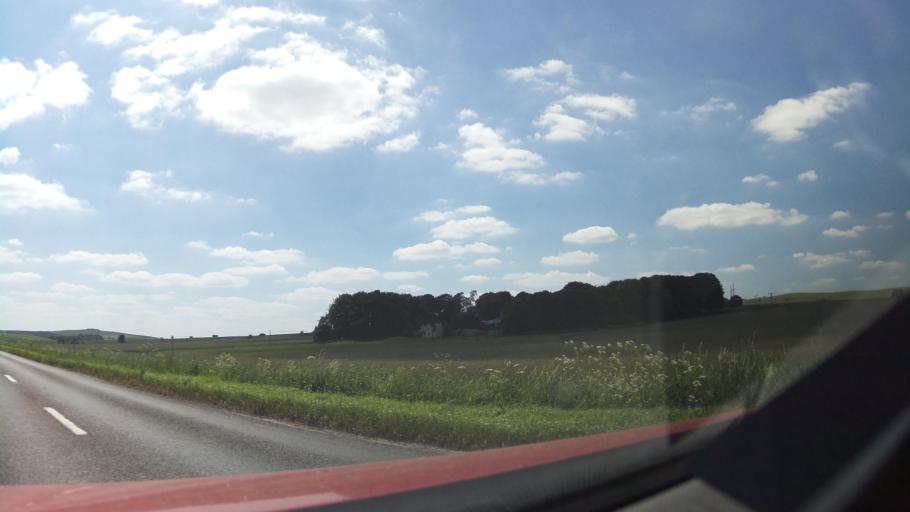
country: GB
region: England
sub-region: Wiltshire
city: Avebury
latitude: 51.3991
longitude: -1.9319
